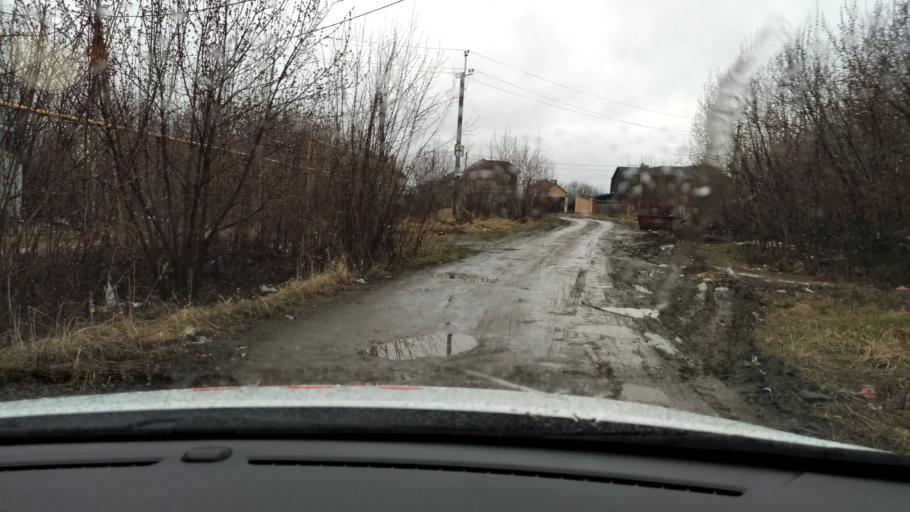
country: RU
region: Tatarstan
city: Staroye Arakchino
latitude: 55.8070
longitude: 48.9302
